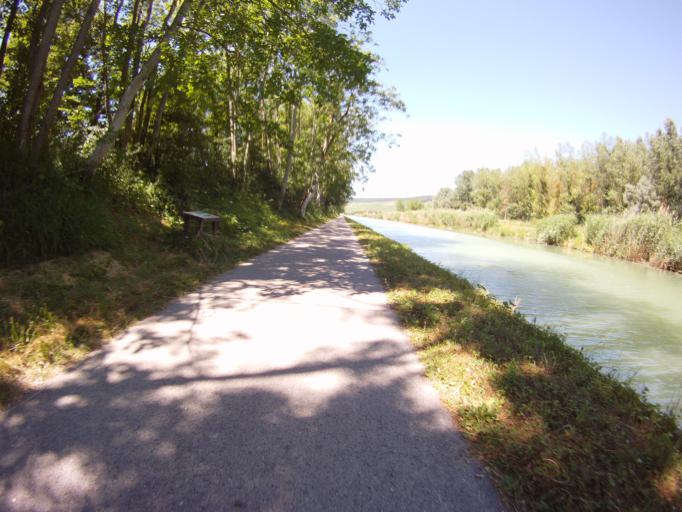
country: FR
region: Champagne-Ardenne
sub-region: Departement de la Marne
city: Dizy
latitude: 49.0636
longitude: 3.9555
